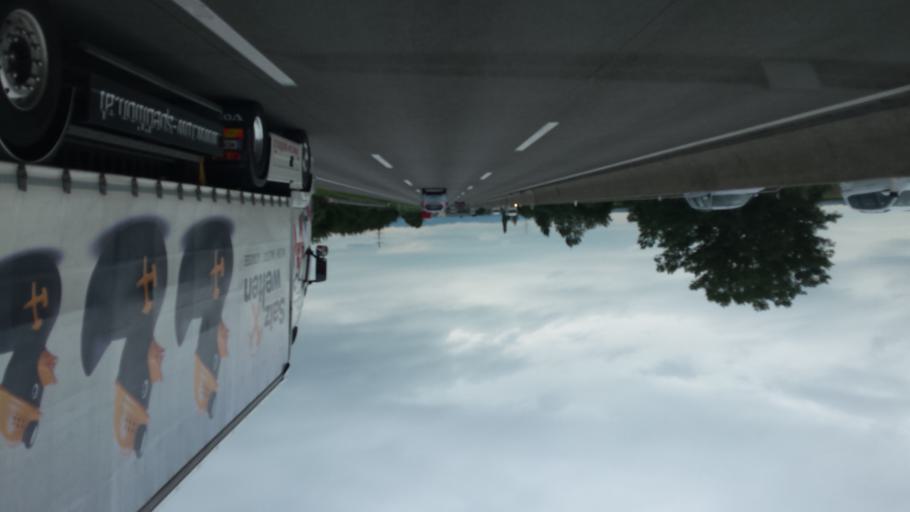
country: AT
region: Lower Austria
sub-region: Politischer Bezirk Sankt Polten
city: Haunoldstein
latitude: 48.1837
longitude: 15.4398
